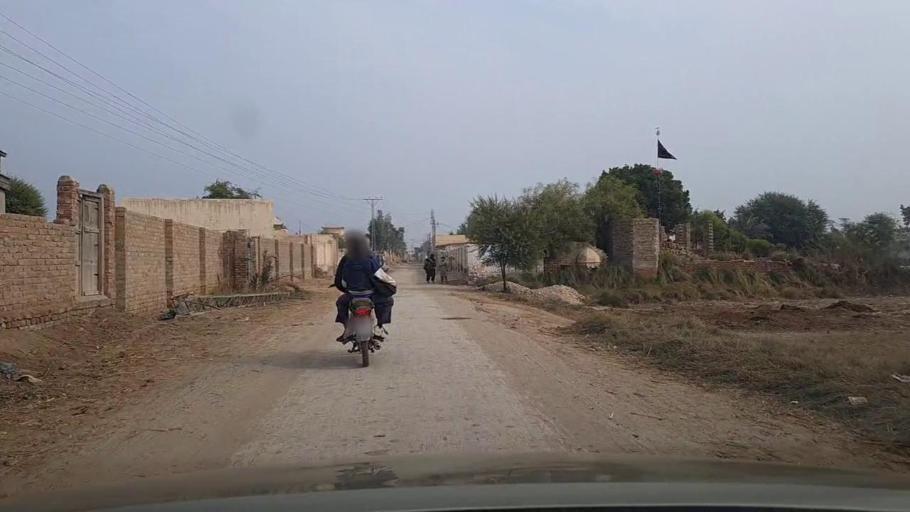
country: PK
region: Sindh
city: Sanghar
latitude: 26.1405
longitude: 68.9622
